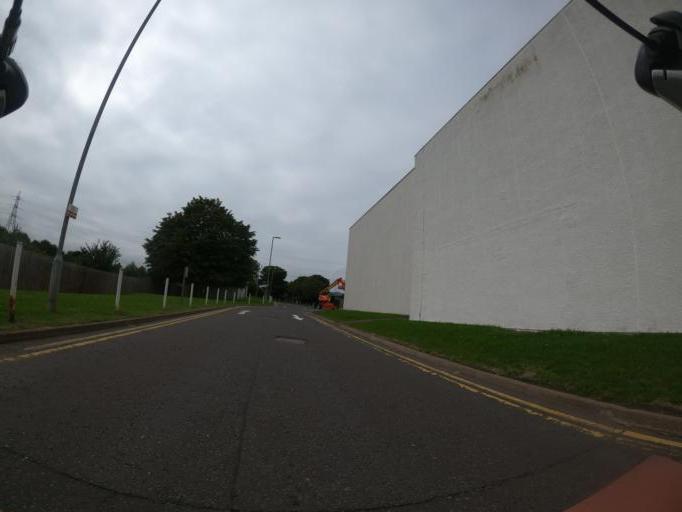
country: GB
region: Scotland
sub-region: East Lothian
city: Musselburgh
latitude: 55.9425
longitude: -3.0968
